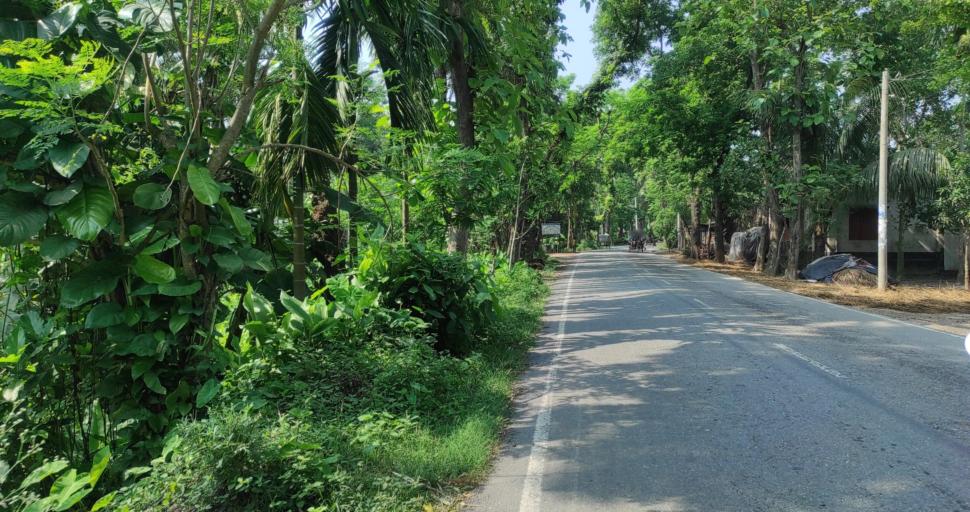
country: BD
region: Rajshahi
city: Ishurdi
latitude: 24.2611
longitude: 89.0492
